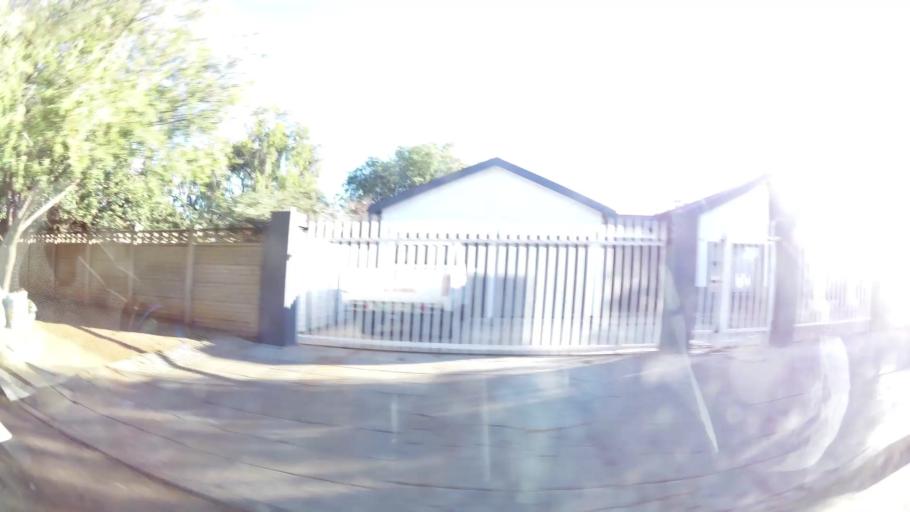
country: ZA
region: Northern Cape
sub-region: Frances Baard District Municipality
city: Kimberley
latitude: -28.7424
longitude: 24.7354
